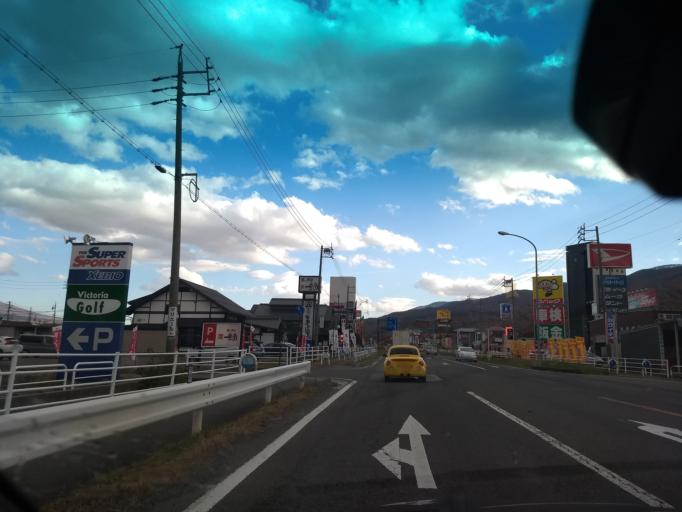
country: JP
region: Nagano
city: Chino
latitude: 36.0040
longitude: 138.1325
